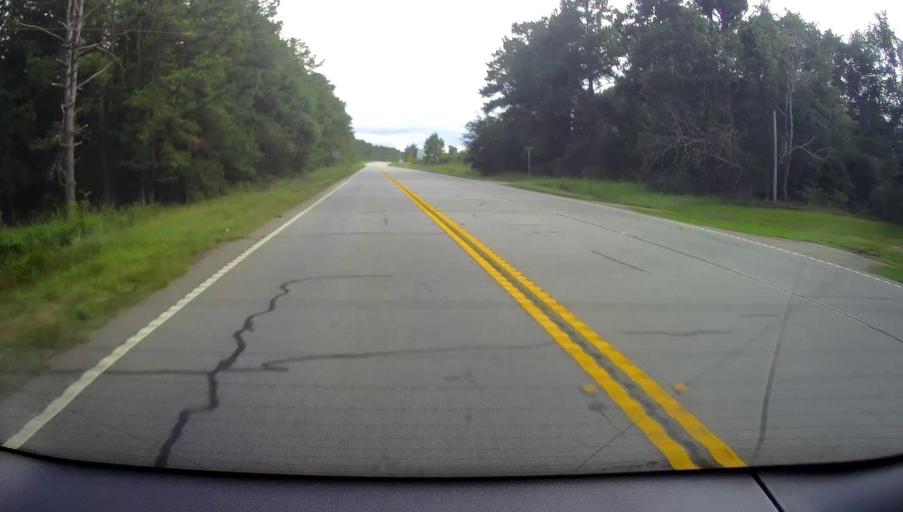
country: US
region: Georgia
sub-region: Meriwether County
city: Greenville
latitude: 33.0158
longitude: -84.5659
